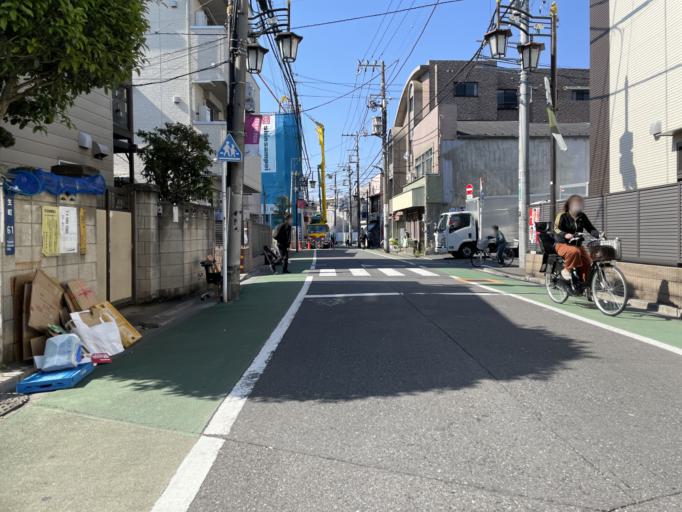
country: JP
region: Saitama
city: Kawaguchi
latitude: 35.7538
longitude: 139.6934
